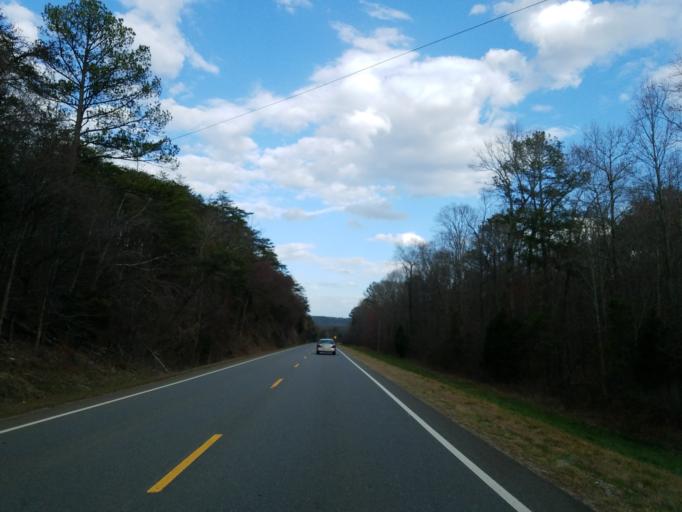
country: US
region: Georgia
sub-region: Bartow County
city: Rydal
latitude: 34.4481
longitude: -84.7330
